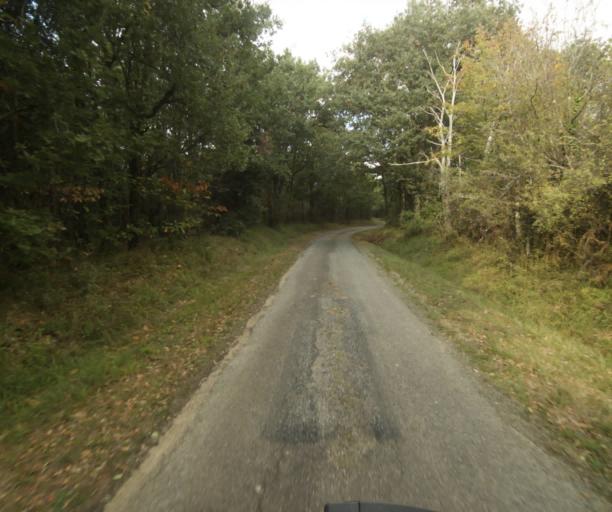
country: FR
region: Midi-Pyrenees
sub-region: Departement de la Haute-Garonne
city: Launac
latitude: 43.8287
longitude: 1.1135
